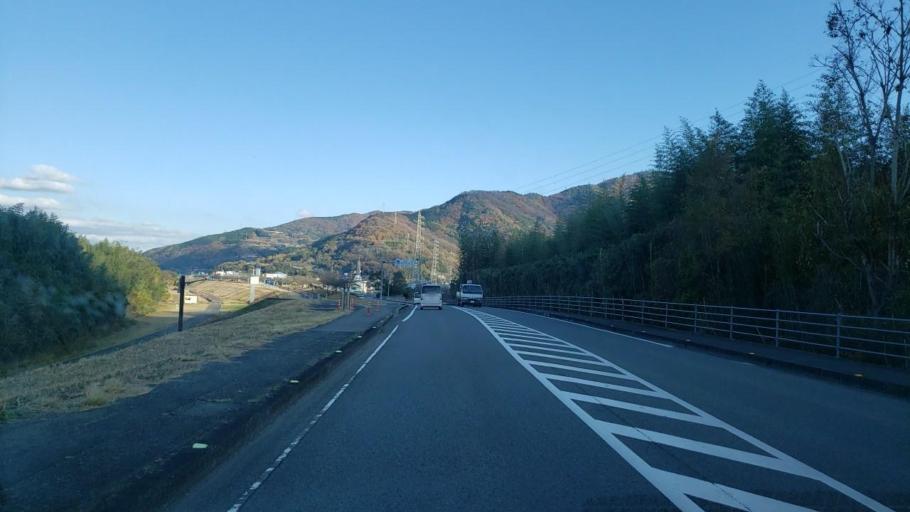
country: JP
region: Tokushima
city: Wakimachi
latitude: 34.0424
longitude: 134.0525
